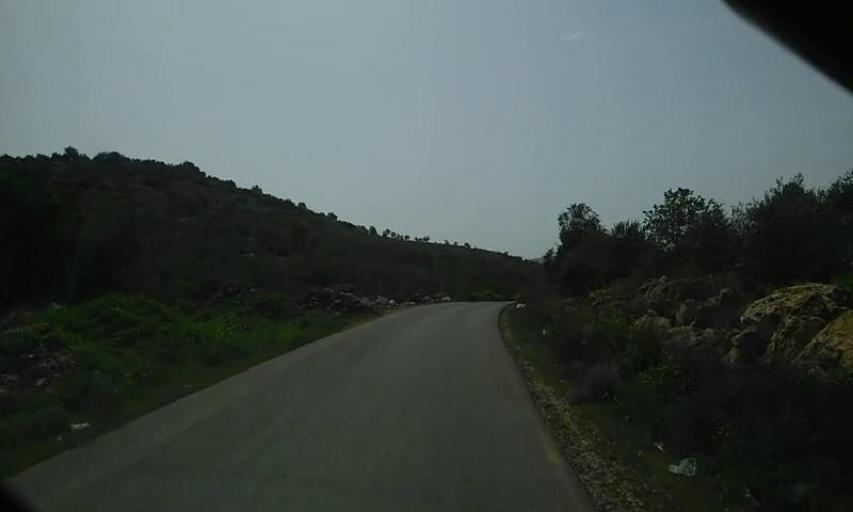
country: PS
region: West Bank
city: Rummanah
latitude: 32.5096
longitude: 35.2101
